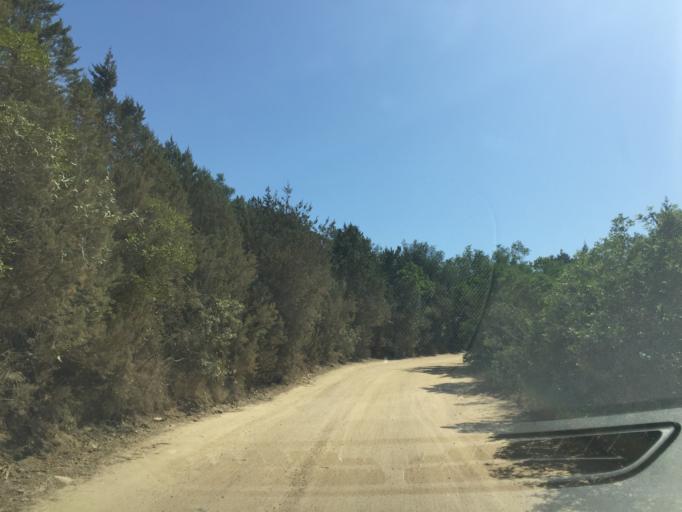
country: IT
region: Sardinia
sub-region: Provincia di Olbia-Tempio
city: San Teodoro
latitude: 40.8404
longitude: 9.7120
